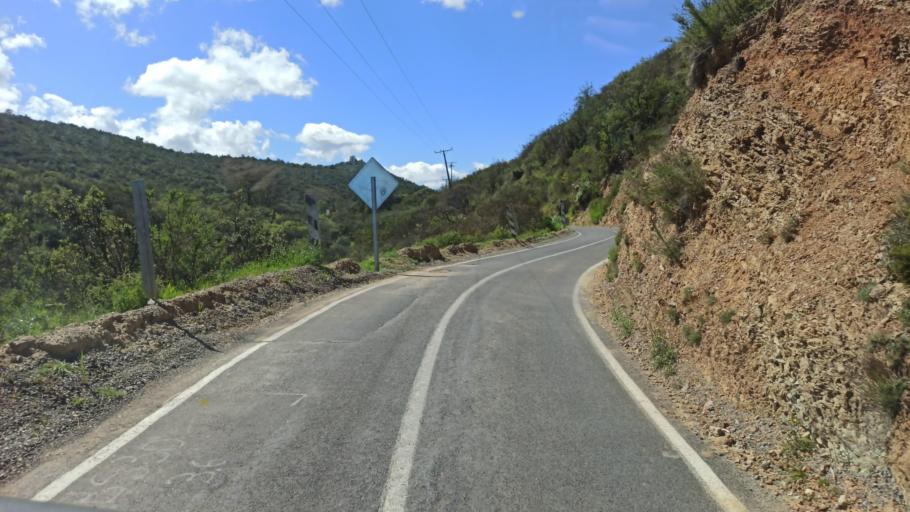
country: CL
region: Valparaiso
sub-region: Provincia de Marga Marga
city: Limache
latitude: -33.2028
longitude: -71.2564
